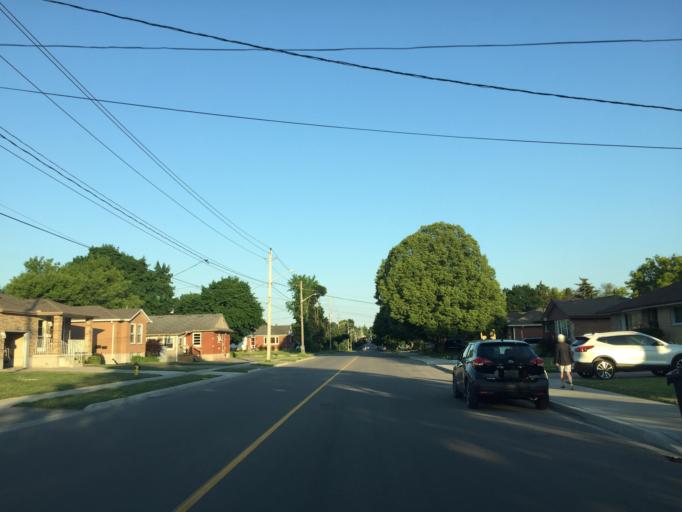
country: CA
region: Ontario
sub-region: Wellington County
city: Guelph
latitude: 43.5611
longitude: -80.2553
